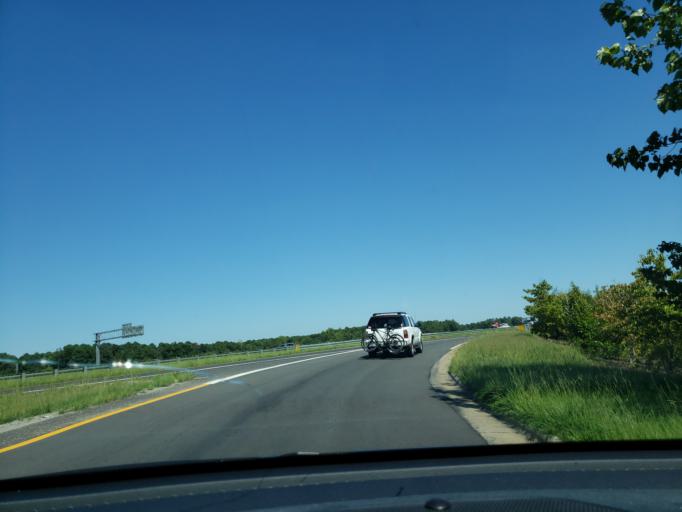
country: US
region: North Carolina
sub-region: Lee County
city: Sanford
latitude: 35.5111
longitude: -79.1896
